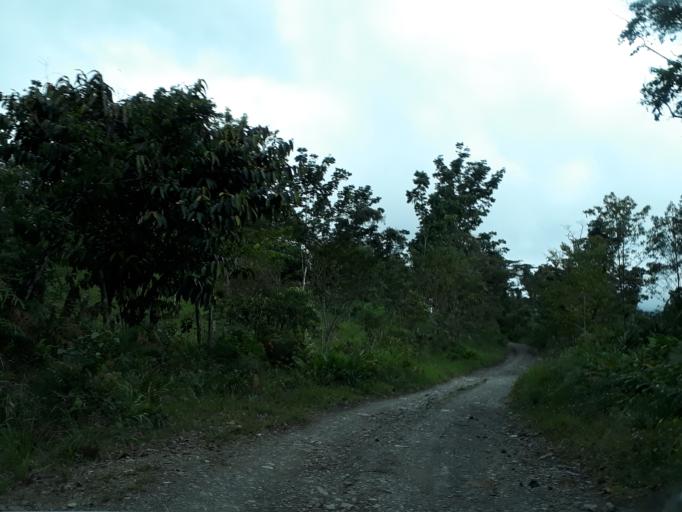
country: CO
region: Boyaca
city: Muzo
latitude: 5.3861
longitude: -74.0979
